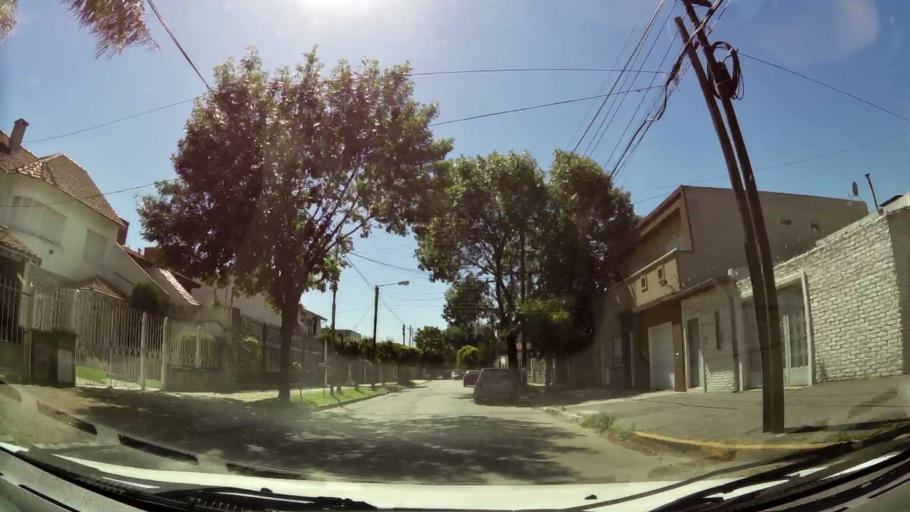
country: AR
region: Buenos Aires
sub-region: Partido de General San Martin
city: General San Martin
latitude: -34.5585
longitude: -58.5529
